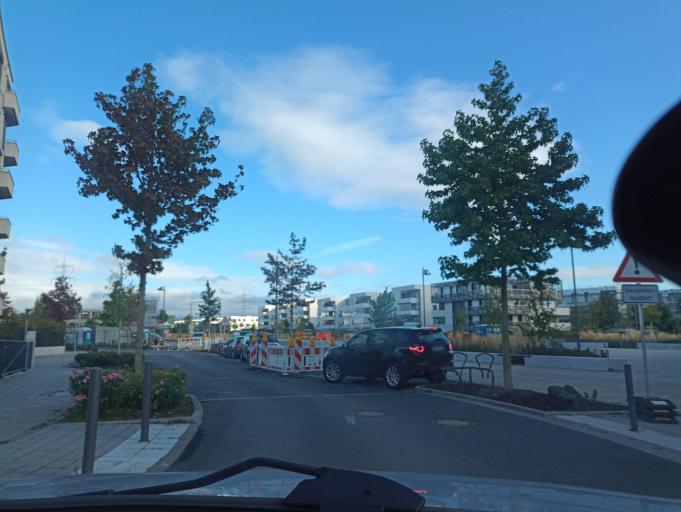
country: DE
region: Hesse
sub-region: Regierungsbezirk Darmstadt
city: Bad Homburg vor der Hoehe
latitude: 50.1783
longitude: 8.6223
